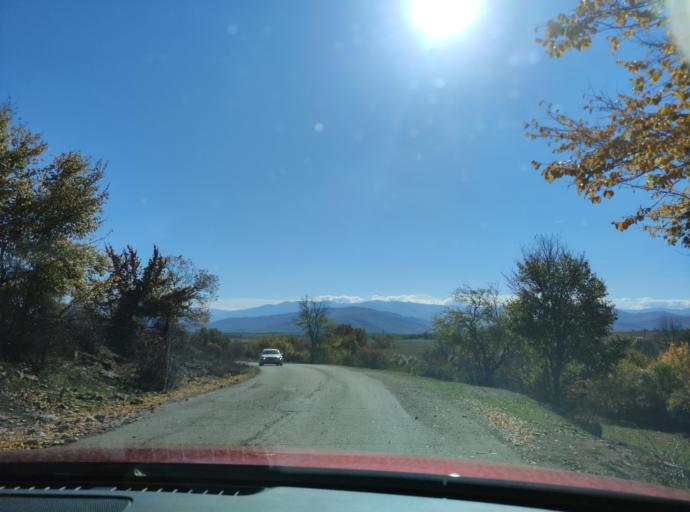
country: BG
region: Montana
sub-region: Obshtina Chiprovtsi
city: Chiprovtsi
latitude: 43.4496
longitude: 23.0461
